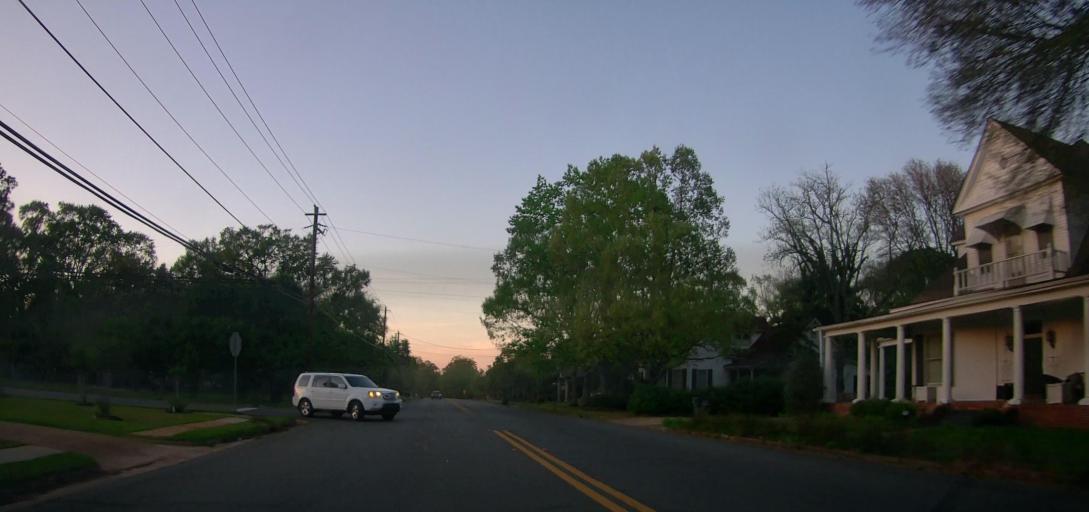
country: US
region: Georgia
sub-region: Marion County
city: Buena Vista
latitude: 32.3215
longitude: -84.5199
